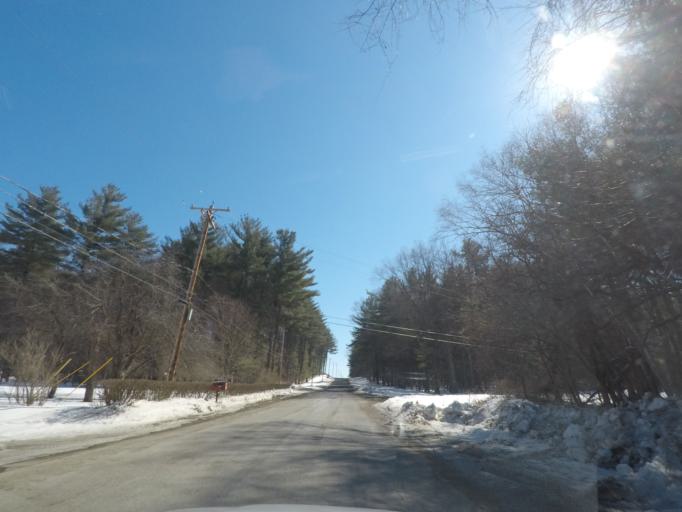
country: US
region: New York
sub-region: Saratoga County
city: Stillwater
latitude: 42.9205
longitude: -73.6204
